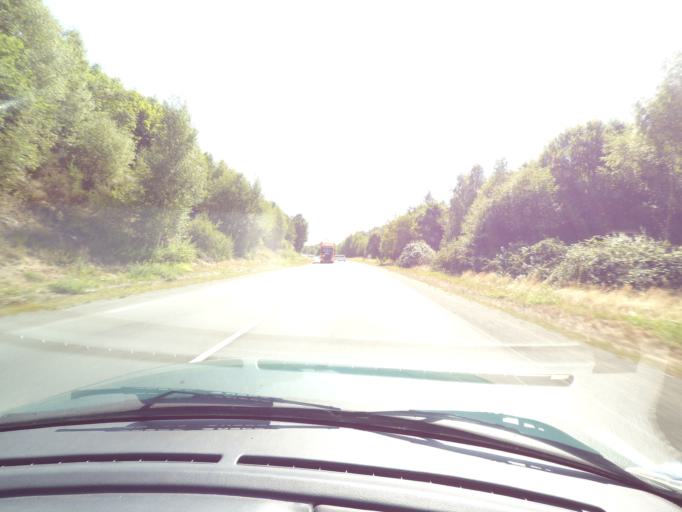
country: FR
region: Limousin
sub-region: Departement de la Haute-Vienne
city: Chaptelat
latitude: 45.8926
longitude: 1.2511
